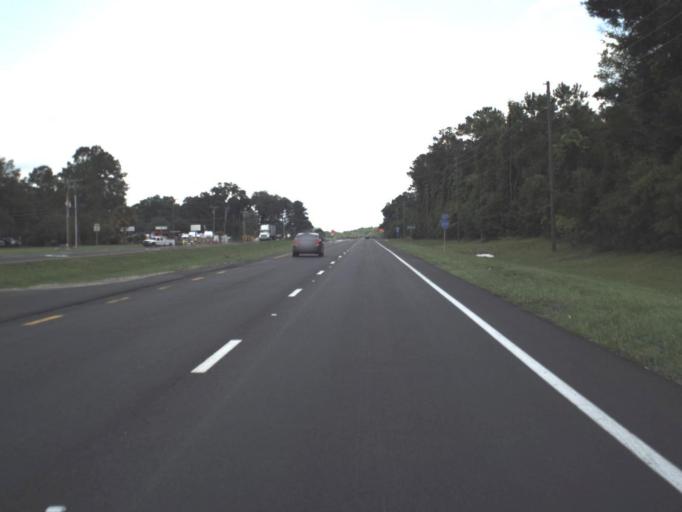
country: US
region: Florida
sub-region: Alachua County
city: Alachua
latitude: 29.7678
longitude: -82.4182
